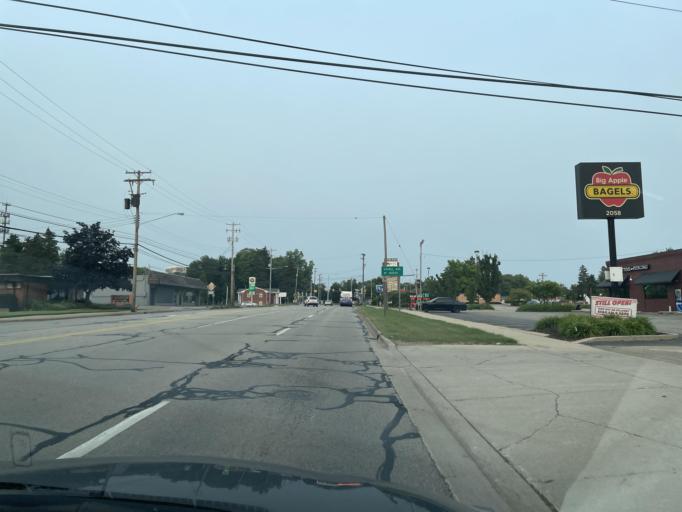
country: US
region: Michigan
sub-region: Kent County
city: Grand Rapids
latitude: 42.9714
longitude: -85.7199
